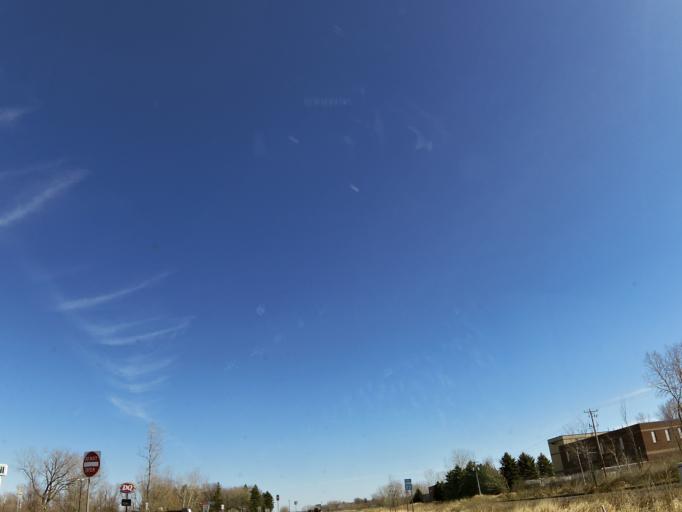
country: US
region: Minnesota
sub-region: Hennepin County
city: Medina
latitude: 45.0459
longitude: -93.5424
